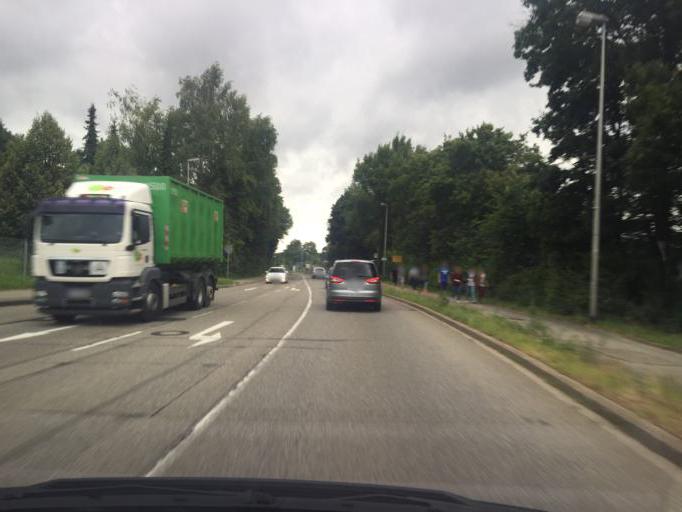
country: DE
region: Baden-Wuerttemberg
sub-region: Karlsruhe Region
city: Bretten
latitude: 49.0257
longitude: 8.7048
